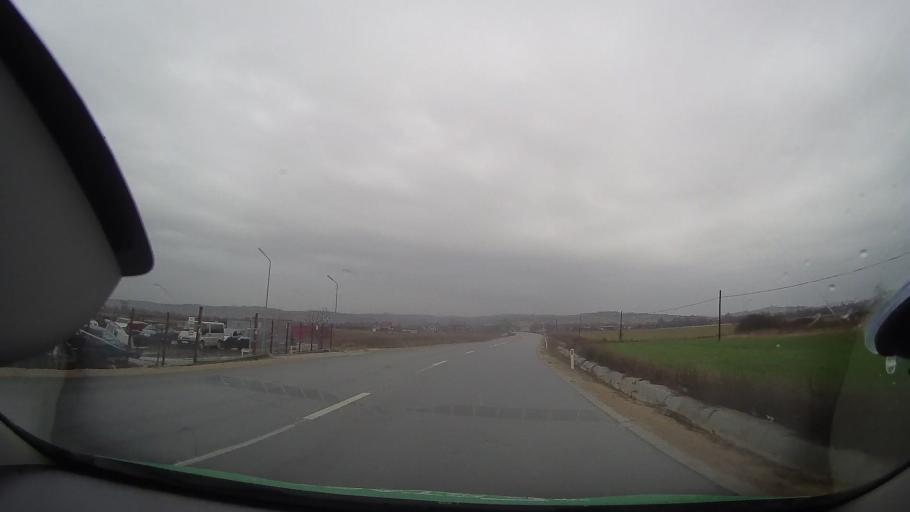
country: RO
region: Bihor
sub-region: Comuna Pocola
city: Pocola
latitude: 46.6893
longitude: 22.2995
